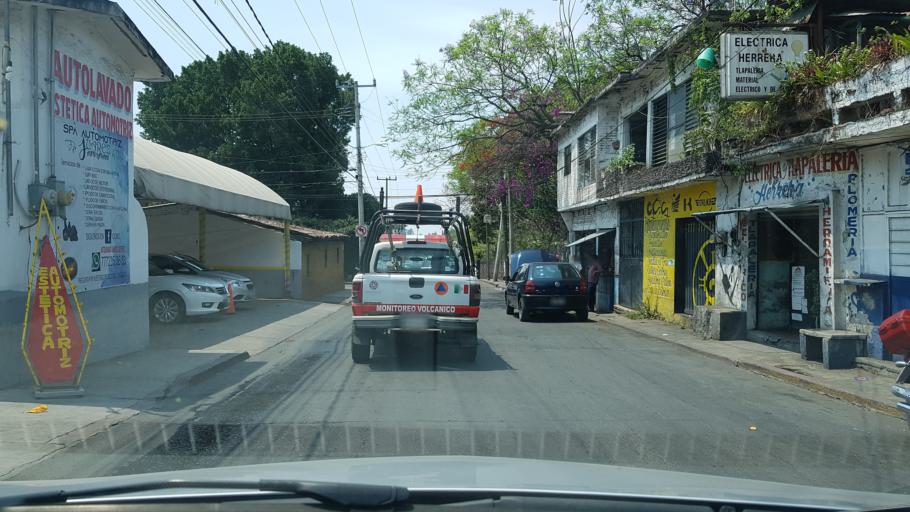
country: MX
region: Morelos
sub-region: Jiutepec
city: Jiutepec
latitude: 18.8872
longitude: -99.1764
